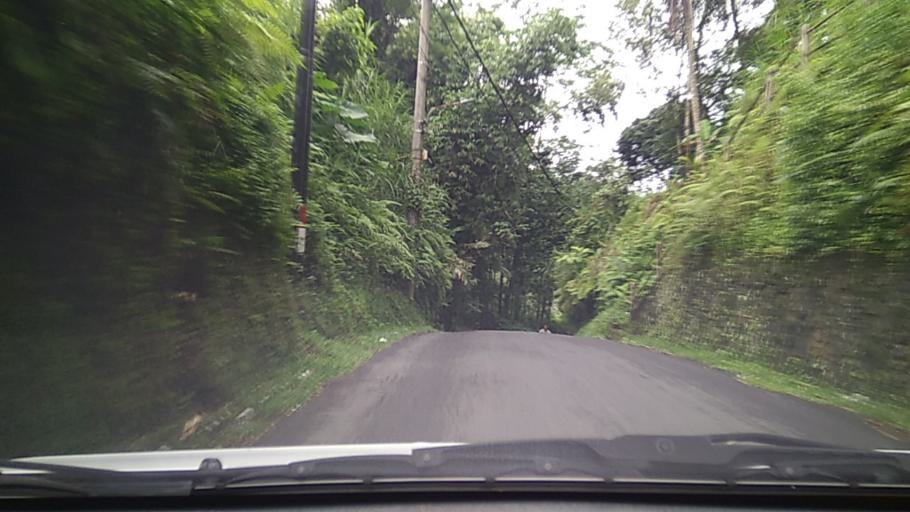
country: ID
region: Bali
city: Banjar Manukayaanyar
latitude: -8.4186
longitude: 115.3068
